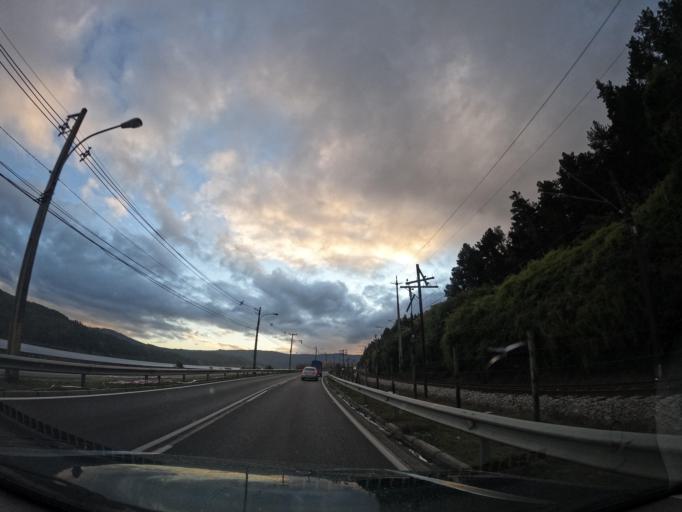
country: CL
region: Biobio
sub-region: Provincia de Concepcion
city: Chiguayante
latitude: -36.9701
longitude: -72.9793
